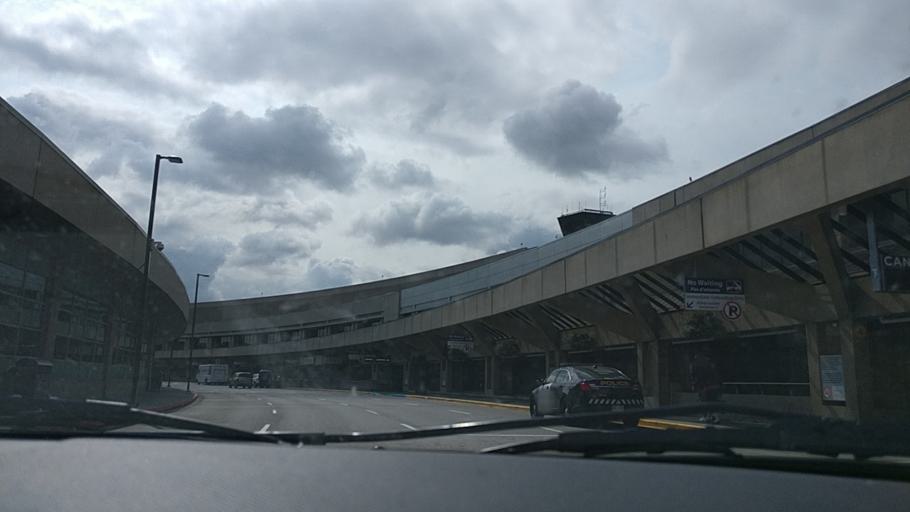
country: CA
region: Alberta
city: Calgary
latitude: 51.1319
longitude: -114.0108
